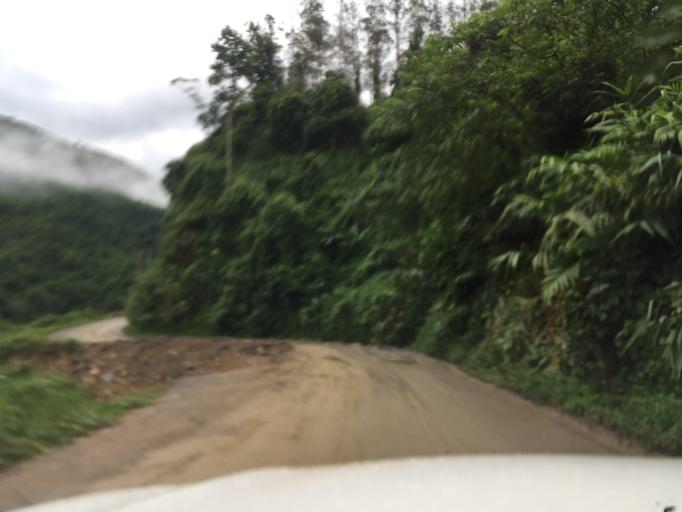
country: LA
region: Oudomxai
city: Muang La
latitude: 21.0020
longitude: 102.2325
